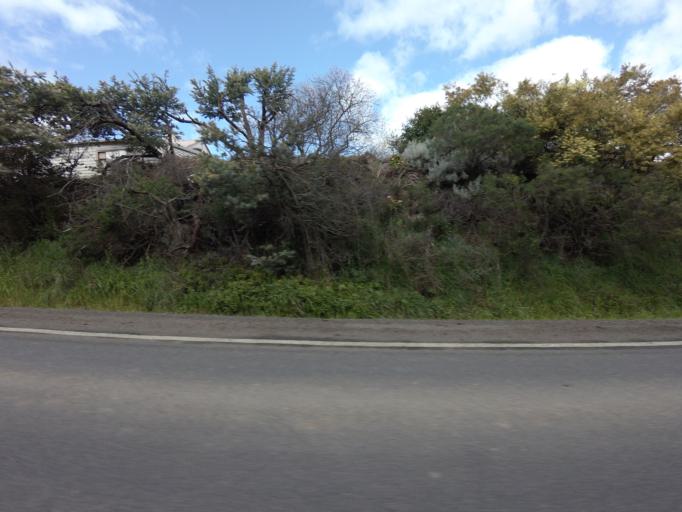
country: AU
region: Tasmania
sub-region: Huon Valley
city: Geeveston
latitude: -43.1365
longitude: 146.9735
